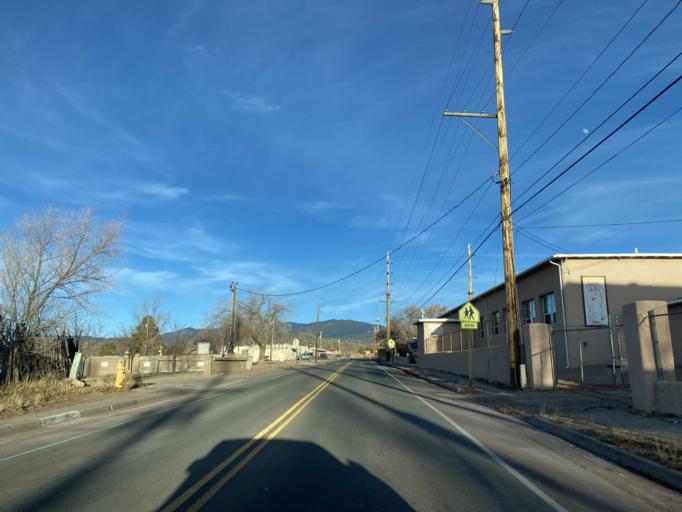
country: US
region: New Mexico
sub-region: Santa Fe County
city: Santa Fe
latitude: 35.6820
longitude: -105.9615
